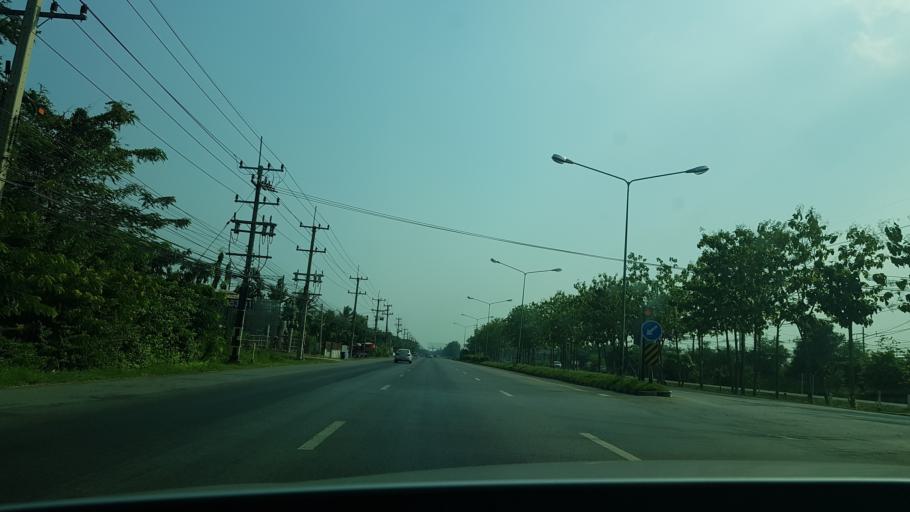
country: TH
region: Phetchaburi
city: Khao Yoi
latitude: 13.2229
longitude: 99.8256
